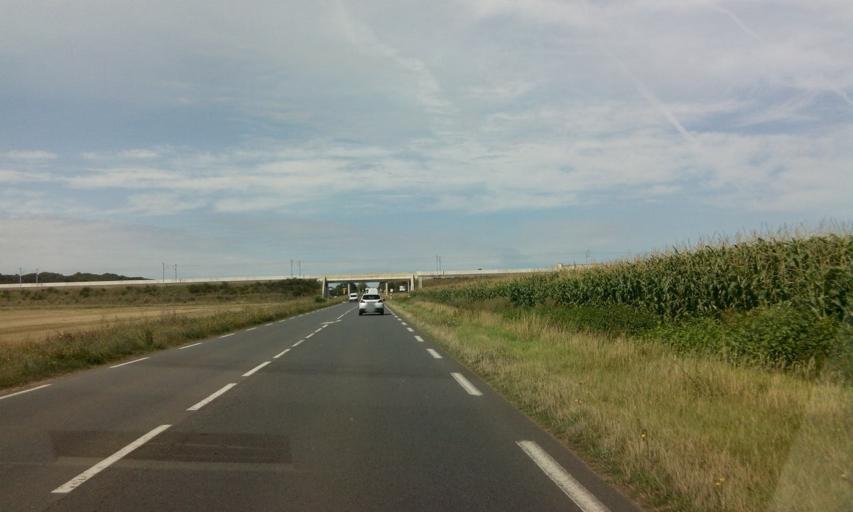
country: FR
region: Poitou-Charentes
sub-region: Departement des Deux-Sevres
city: Sauze-Vaussais
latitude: 46.1351
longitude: 0.1345
